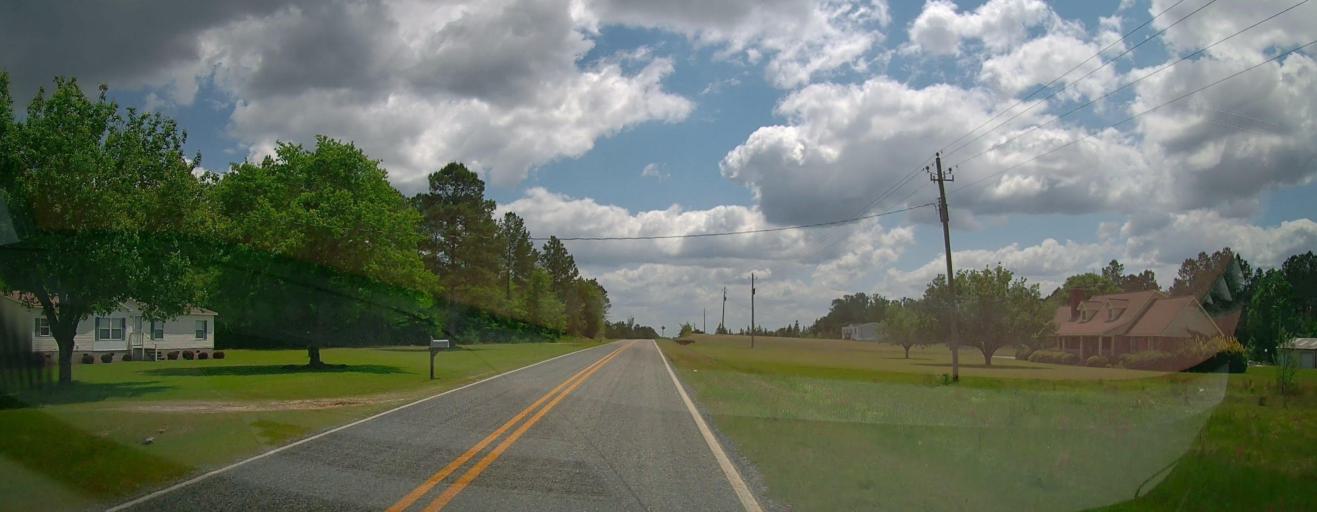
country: US
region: Georgia
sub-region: Laurens County
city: East Dublin
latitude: 32.5860
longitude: -82.7865
